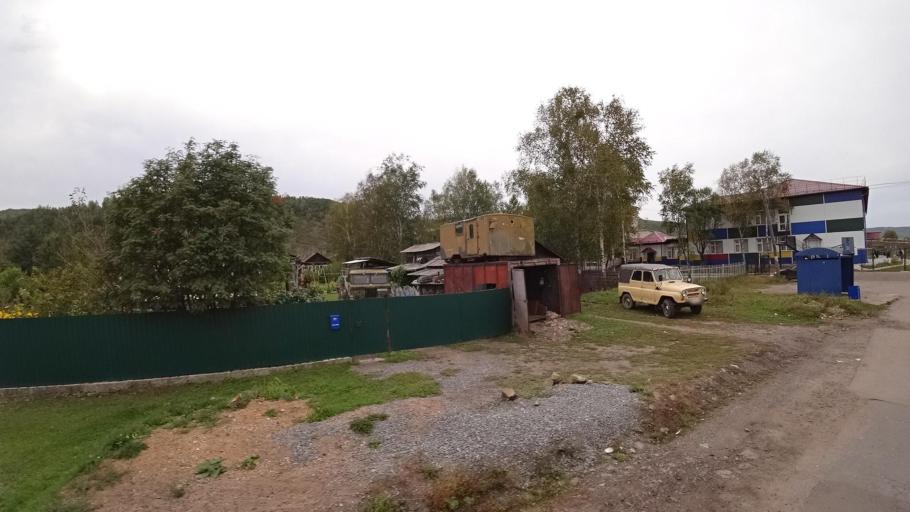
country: RU
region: Jewish Autonomous Oblast
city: Khingansk
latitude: 49.0277
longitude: 131.0490
